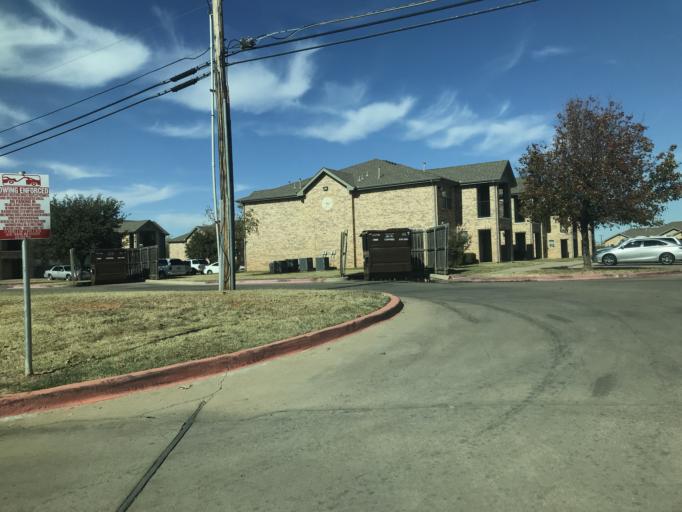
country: US
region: Texas
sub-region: Taylor County
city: Abilene
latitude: 32.4866
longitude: -99.7471
